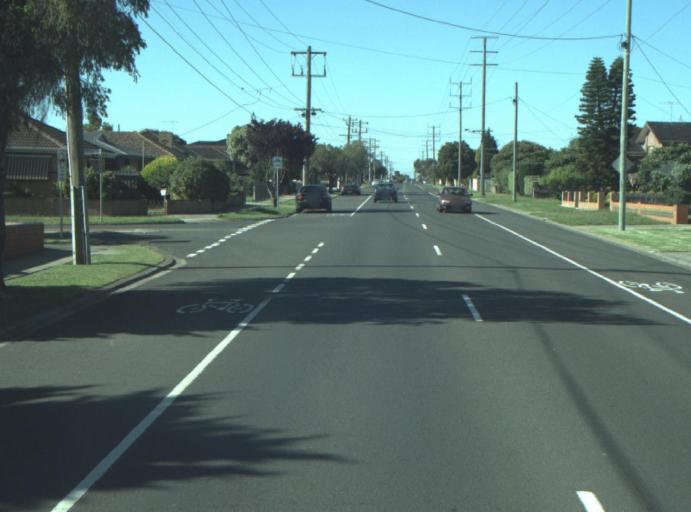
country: AU
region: Victoria
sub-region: Greater Geelong
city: Bell Post Hill
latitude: -38.0979
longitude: 144.3235
